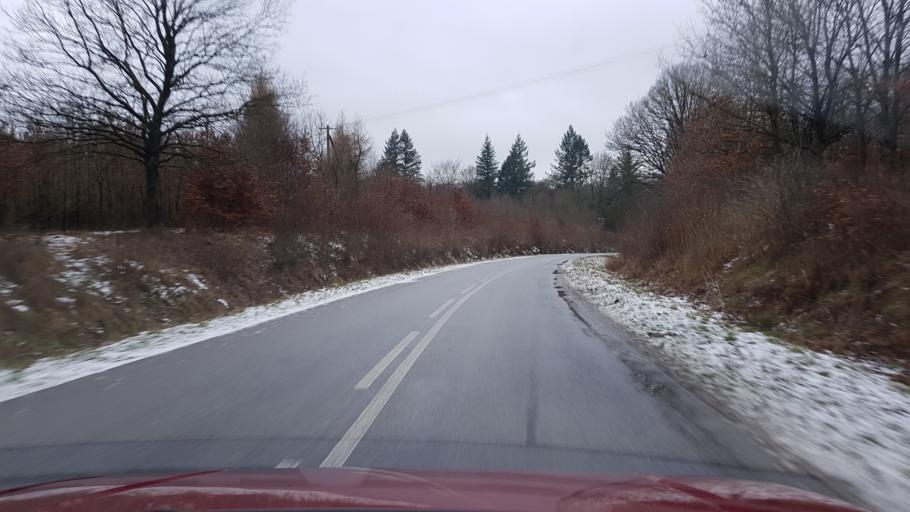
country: PL
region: West Pomeranian Voivodeship
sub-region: Powiat gryficki
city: Ploty
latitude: 53.7178
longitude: 15.3021
